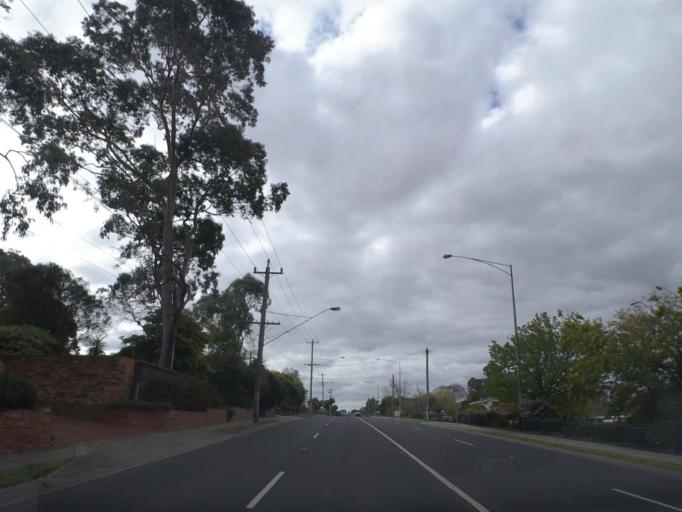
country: AU
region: Victoria
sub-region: Manningham
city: Templestowe Lower
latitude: -37.7778
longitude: 145.1135
